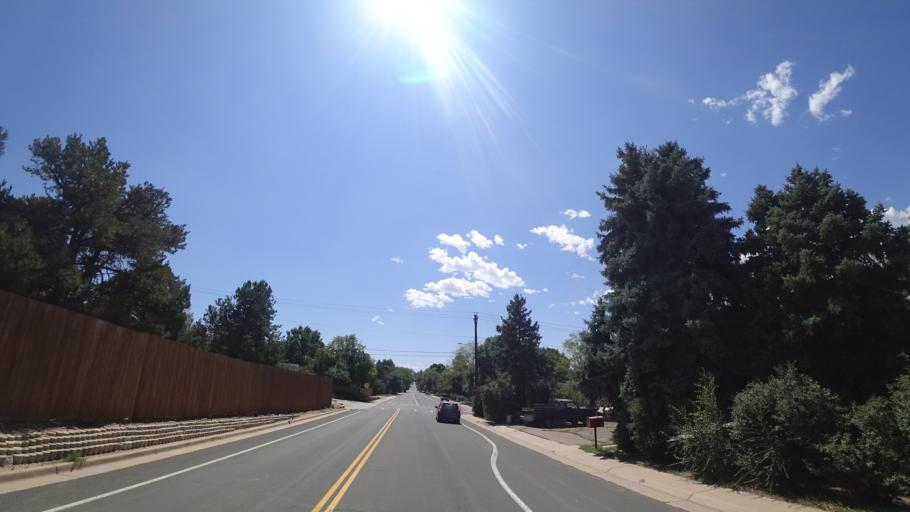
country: US
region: Colorado
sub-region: Arapahoe County
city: Littleton
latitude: 39.6029
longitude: -105.0022
